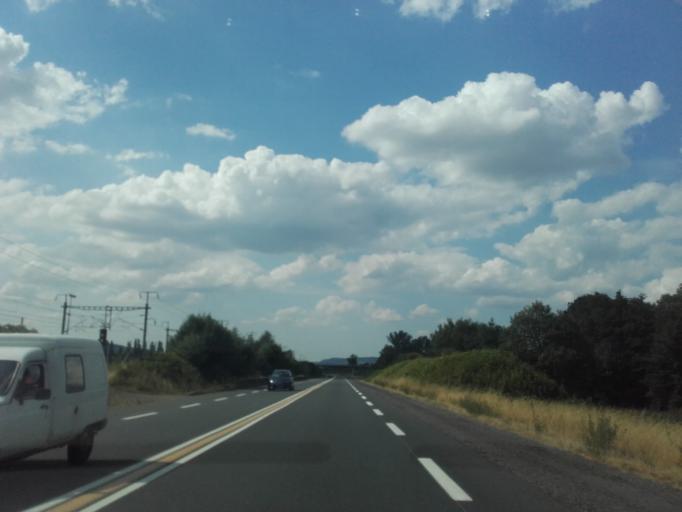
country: FR
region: Bourgogne
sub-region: Departement de Saone-et-Loire
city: Charnay-les-Macon
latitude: 46.2955
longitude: 4.7709
